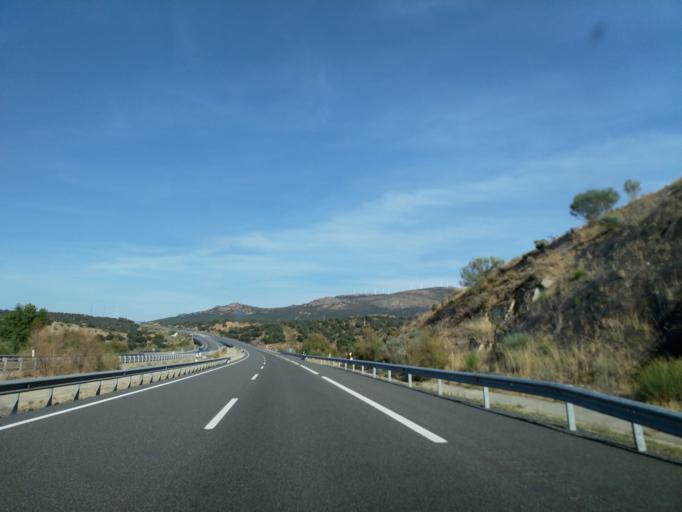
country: ES
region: Castille and Leon
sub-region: Provincia de Avila
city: Mediana de Voltoya
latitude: 40.7160
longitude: -4.5447
